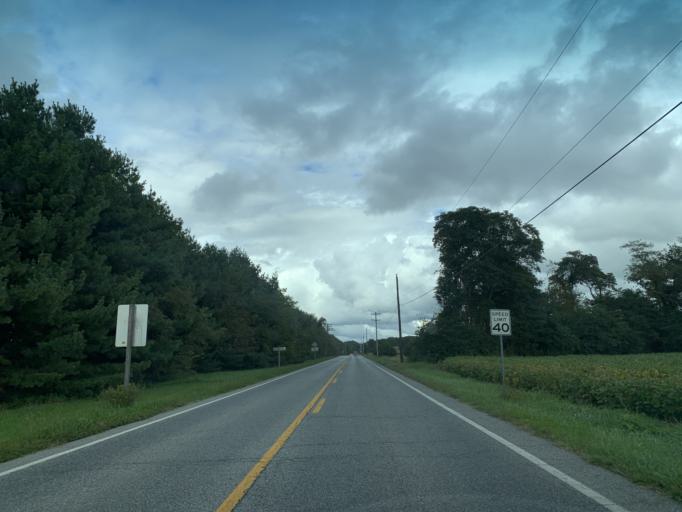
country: US
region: Maryland
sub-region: Caroline County
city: Ridgely
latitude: 39.0361
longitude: -75.8733
